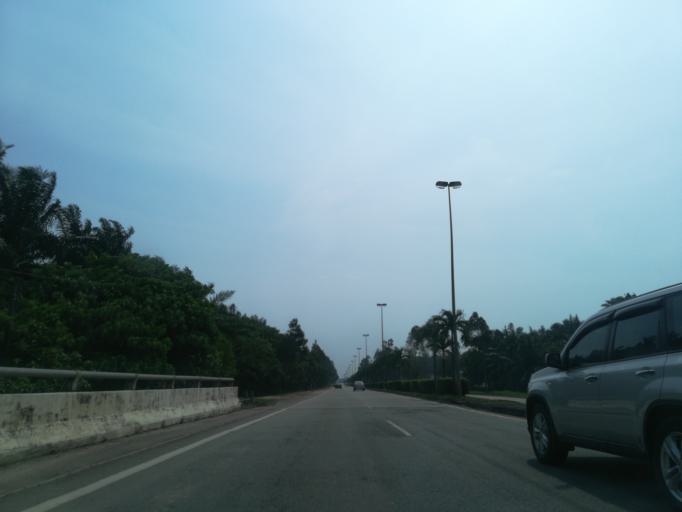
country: MY
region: Penang
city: Tasek Glugor
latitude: 5.4366
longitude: 100.5554
